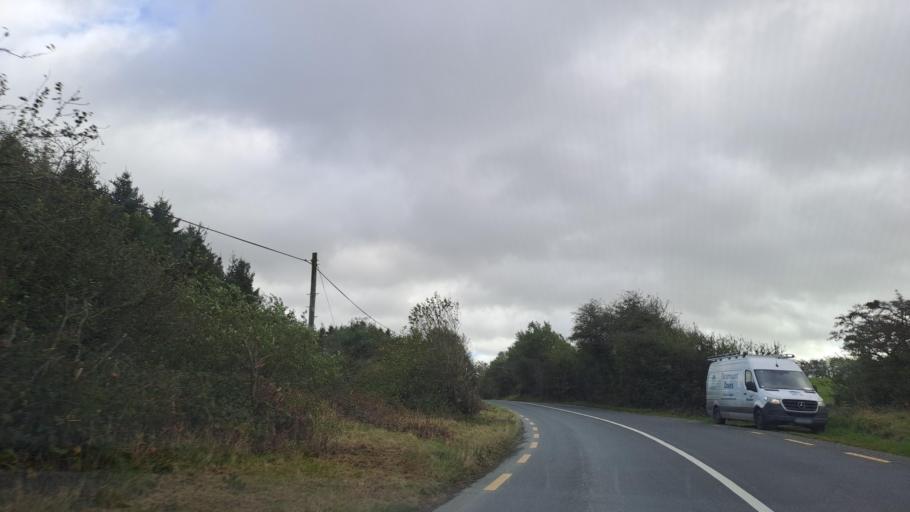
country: IE
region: Ulster
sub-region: An Cabhan
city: Kingscourt
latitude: 53.9290
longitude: -6.8799
